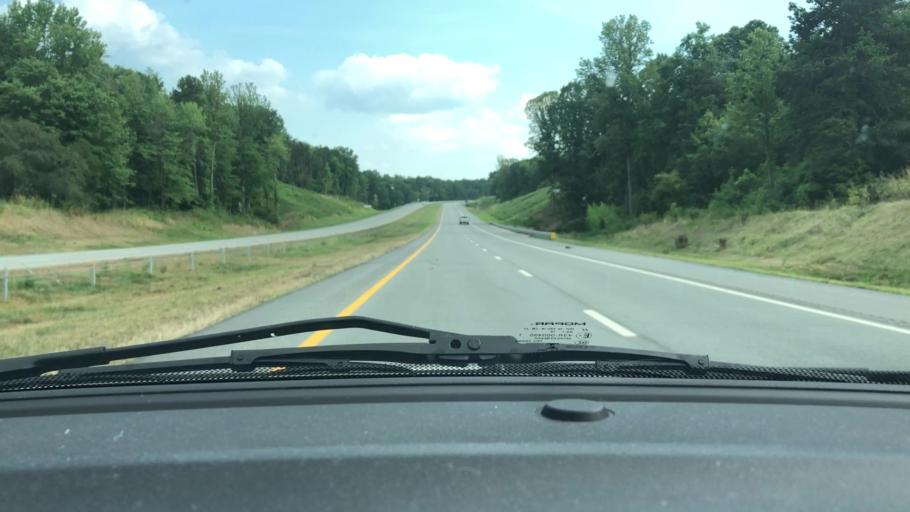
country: US
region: North Carolina
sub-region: Guilford County
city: Oak Ridge
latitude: 36.1522
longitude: -79.9593
